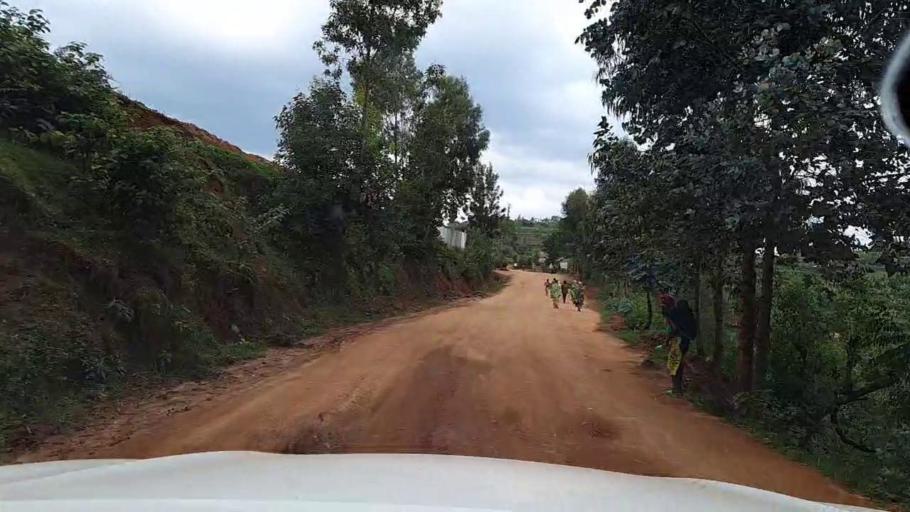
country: BI
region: Kayanza
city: Kayanza
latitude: -2.7120
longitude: 29.5336
